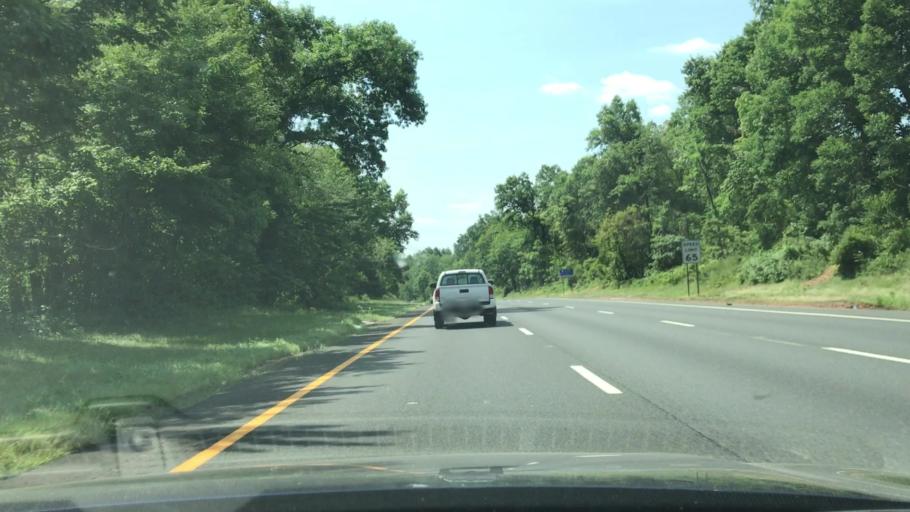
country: US
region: New Jersey
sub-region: Somerset County
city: Finderne
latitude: 40.5787
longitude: -74.5729
